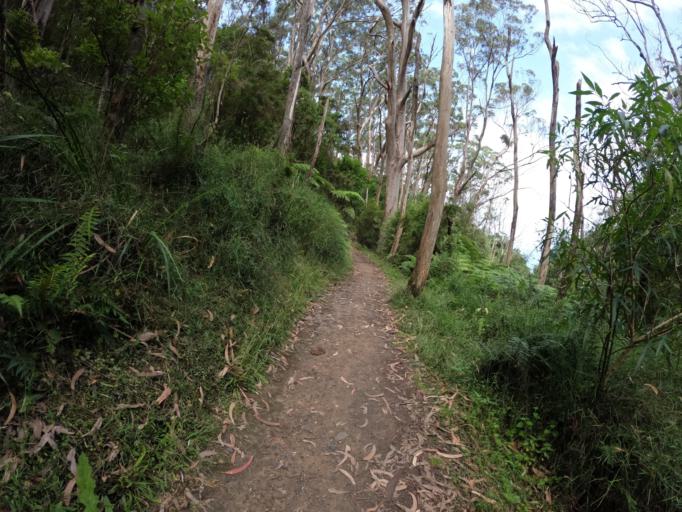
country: AU
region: Victoria
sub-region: Colac-Otway
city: Apollo Bay
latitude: -38.7894
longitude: 143.6213
